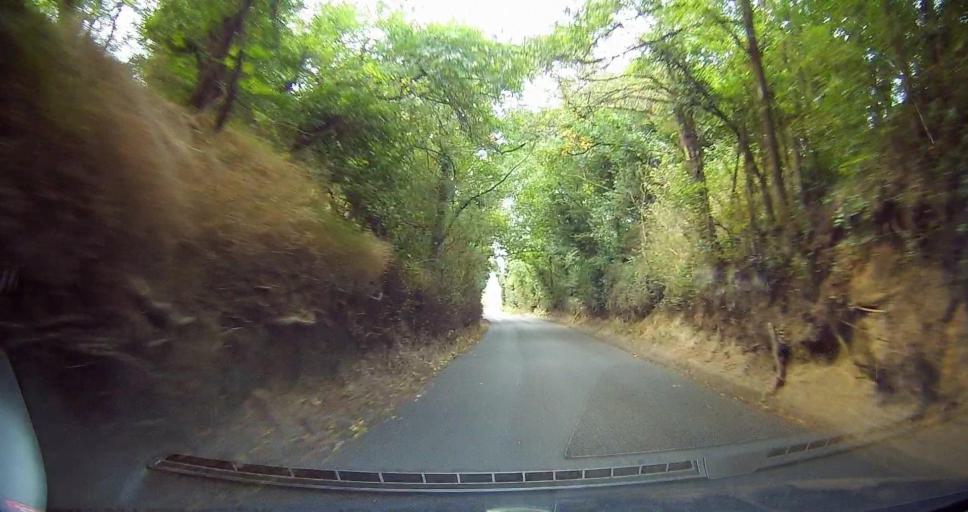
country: GB
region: England
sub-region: Kent
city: Longfield
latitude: 51.4154
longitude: 0.2856
